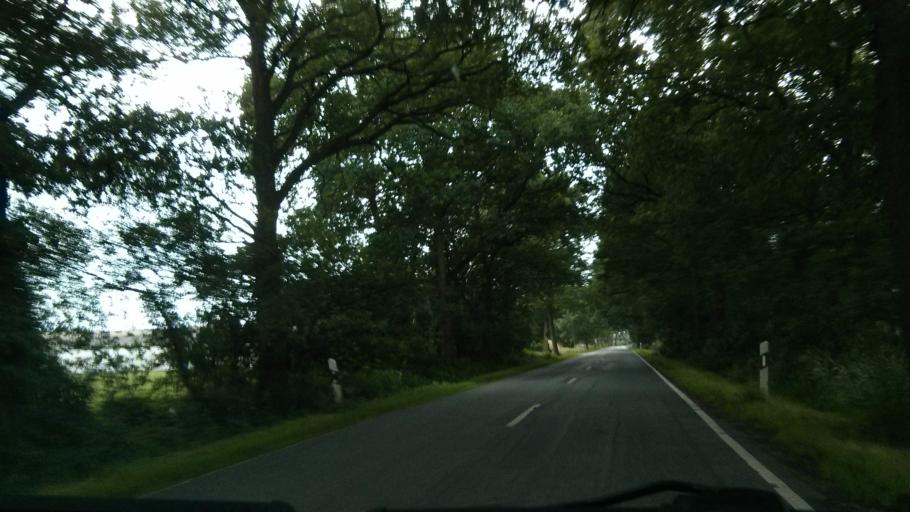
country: DE
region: Lower Saxony
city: Beverstedt
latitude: 53.4705
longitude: 8.8496
